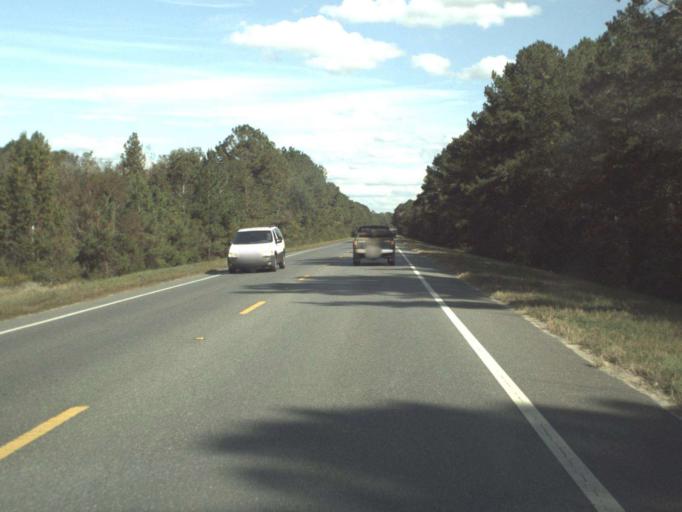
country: US
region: Florida
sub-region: Washington County
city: Chipley
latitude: 30.7776
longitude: -85.6012
